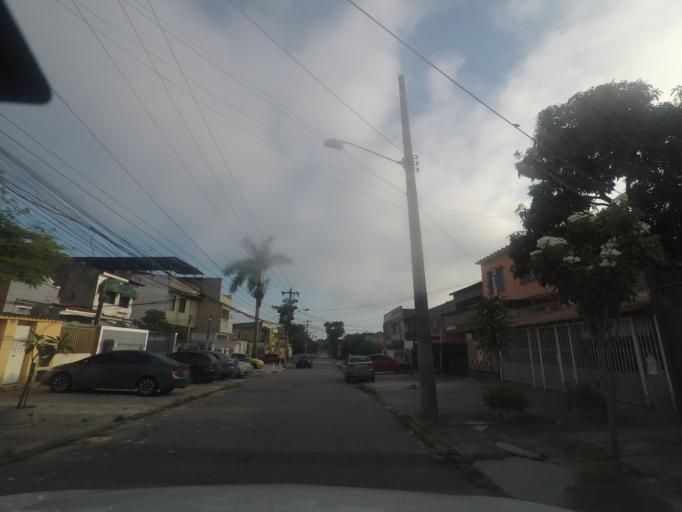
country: BR
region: Rio de Janeiro
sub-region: Duque De Caxias
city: Duque de Caxias
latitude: -22.8392
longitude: -43.2730
